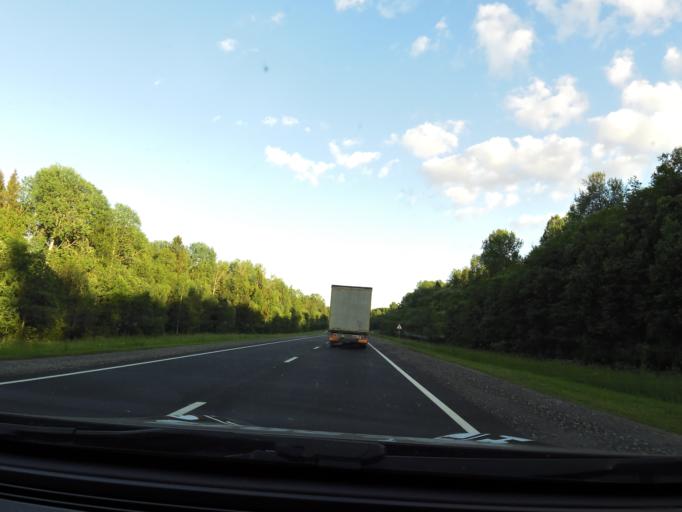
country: RU
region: Vologda
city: Gryazovets
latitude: 58.9701
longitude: 40.1542
